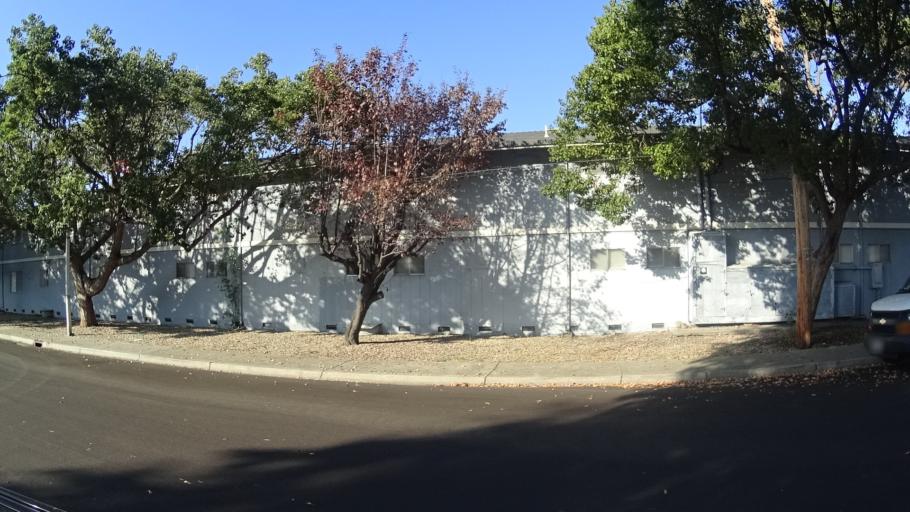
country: US
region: California
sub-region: Santa Clara County
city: Santa Clara
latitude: 37.3510
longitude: -121.9708
